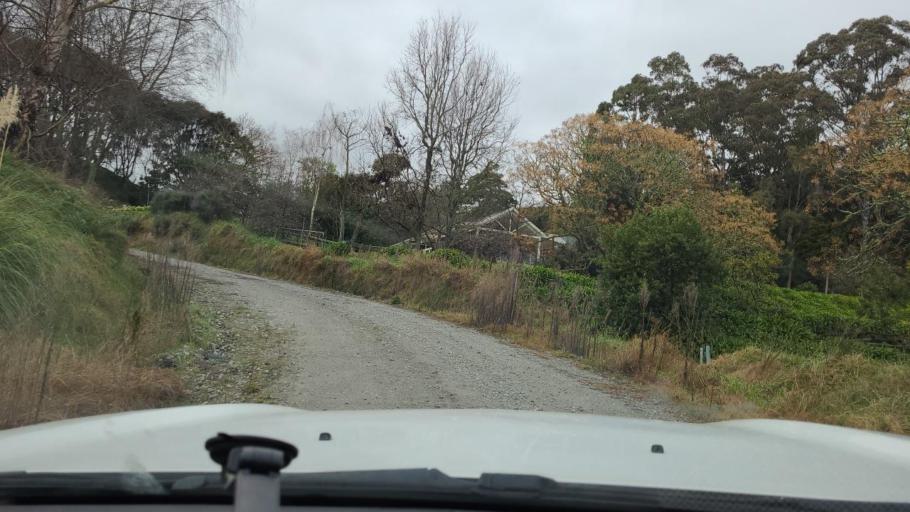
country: NZ
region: Gisborne
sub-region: Gisborne District
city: Gisborne
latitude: -38.5664
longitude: 177.7947
